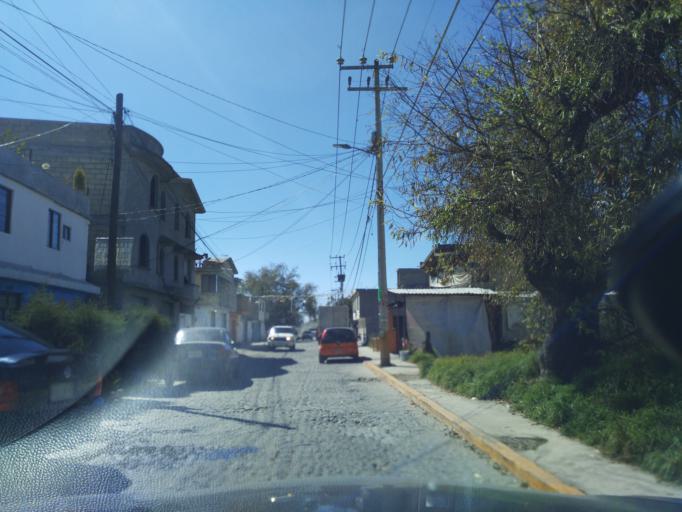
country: MX
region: Morelos
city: Ocoyoacac
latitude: 19.2682
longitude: -99.4628
